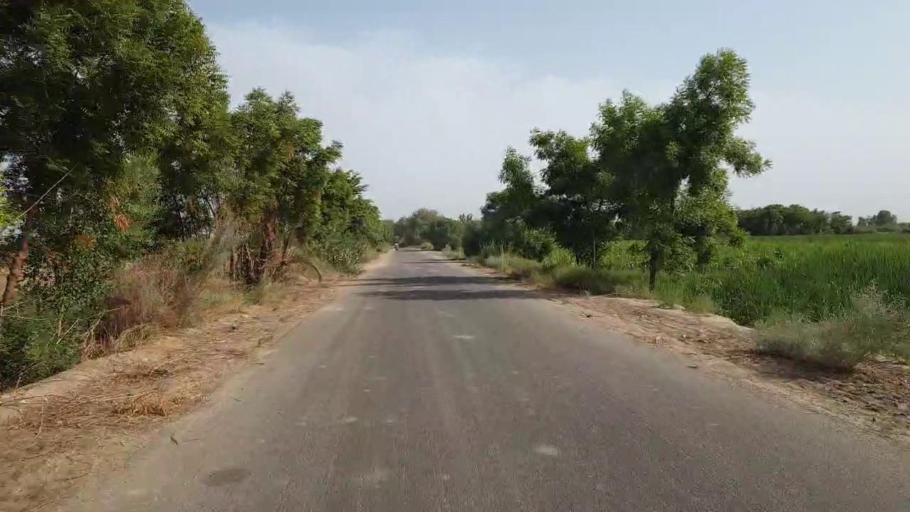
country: PK
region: Sindh
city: Sakrand
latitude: 26.2544
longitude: 68.2848
